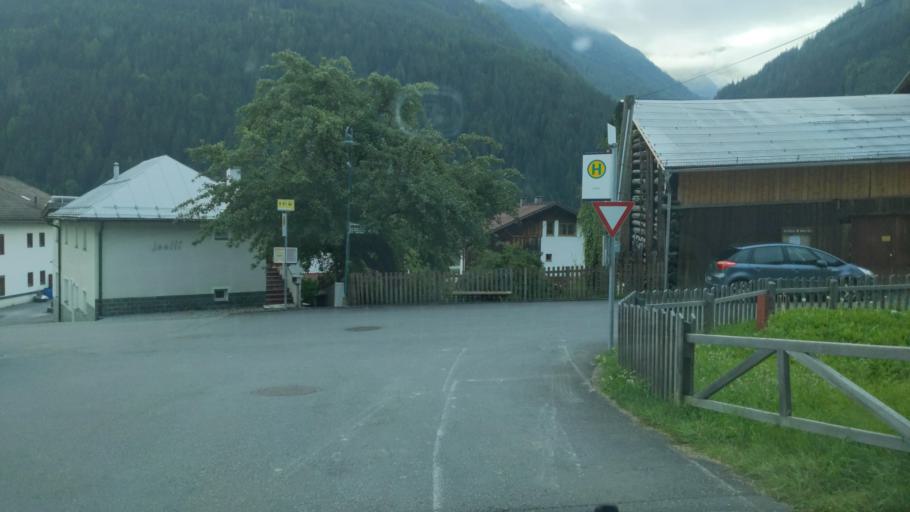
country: AT
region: Tyrol
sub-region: Politischer Bezirk Landeck
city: Flirsch
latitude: 47.1495
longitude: 10.3446
